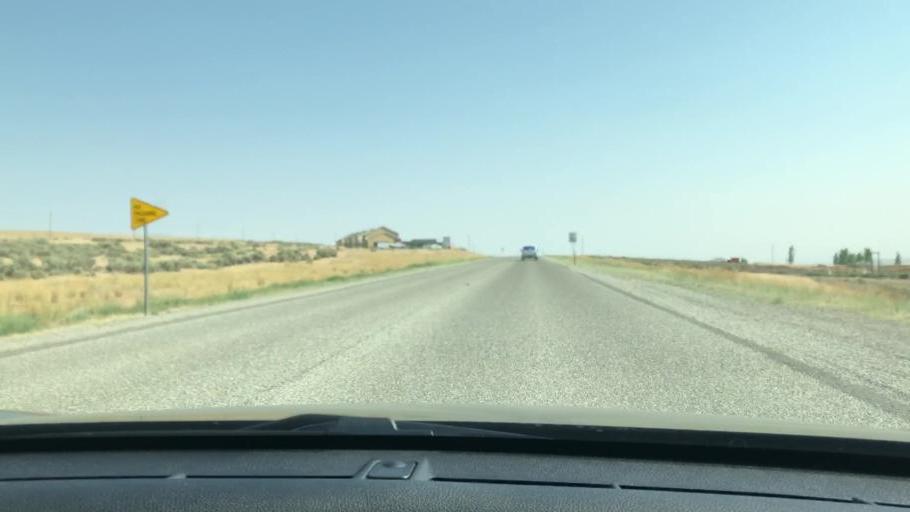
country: US
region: Nevada
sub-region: Humboldt County
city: Winnemucca
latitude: 40.9959
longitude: -117.7356
